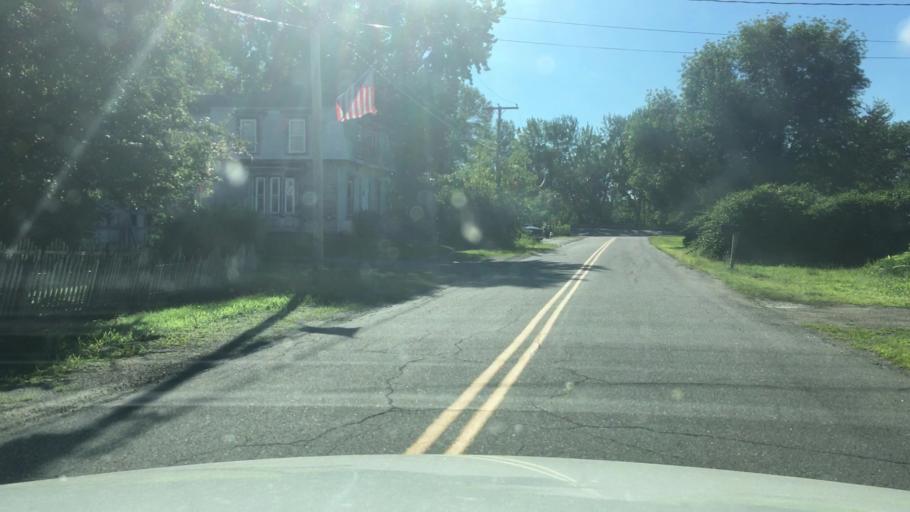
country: US
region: Maine
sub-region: Penobscot County
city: Howland
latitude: 45.1852
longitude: -68.6146
